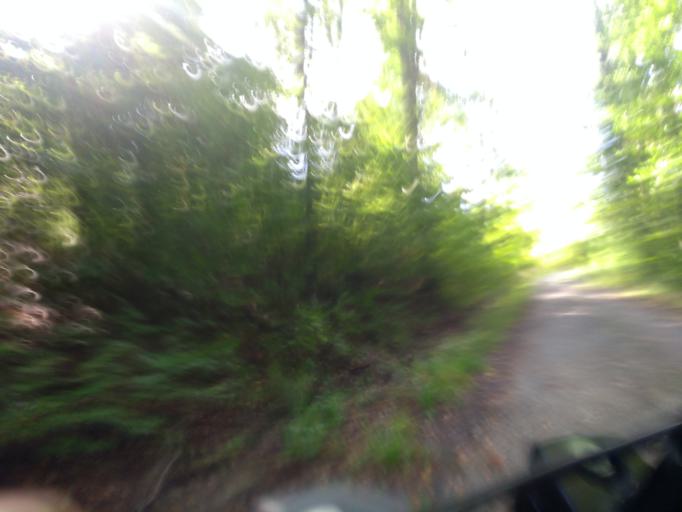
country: DE
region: Baden-Wuerttemberg
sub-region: Karlsruhe Region
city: Birkenfeld
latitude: 48.9055
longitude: 8.6251
